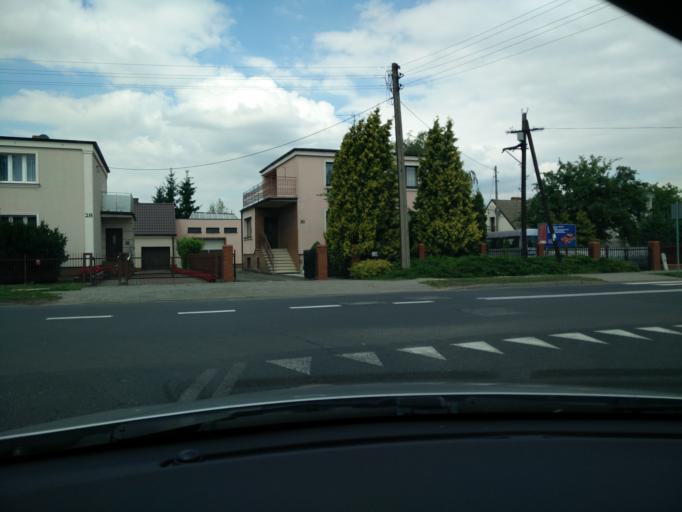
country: PL
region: Greater Poland Voivodeship
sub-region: Powiat sredzki
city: Sroda Wielkopolska
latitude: 52.2300
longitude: 17.2895
